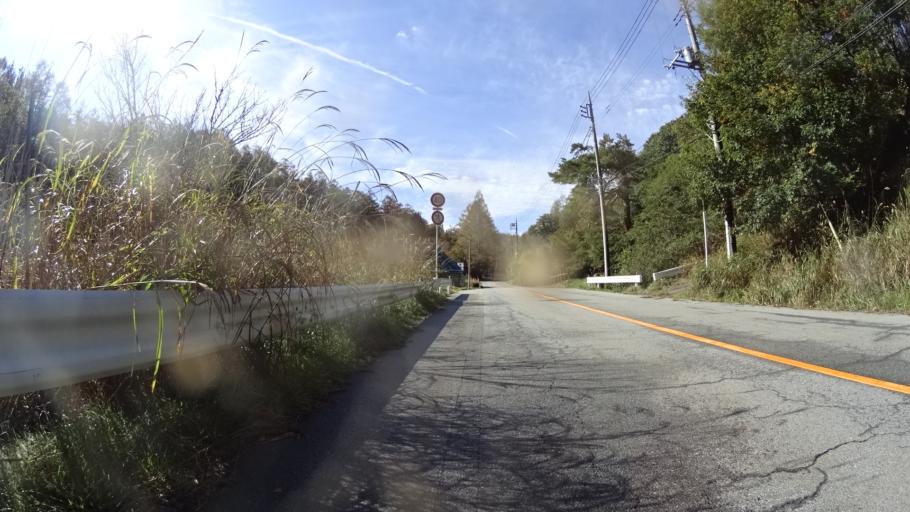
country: JP
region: Yamanashi
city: Enzan
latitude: 35.8002
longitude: 138.8187
